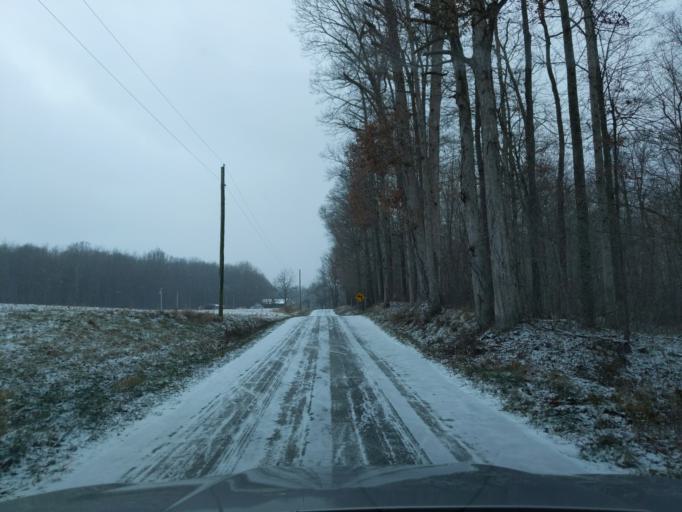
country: US
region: Indiana
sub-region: Decatur County
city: Westport
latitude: 39.2339
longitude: -85.4913
